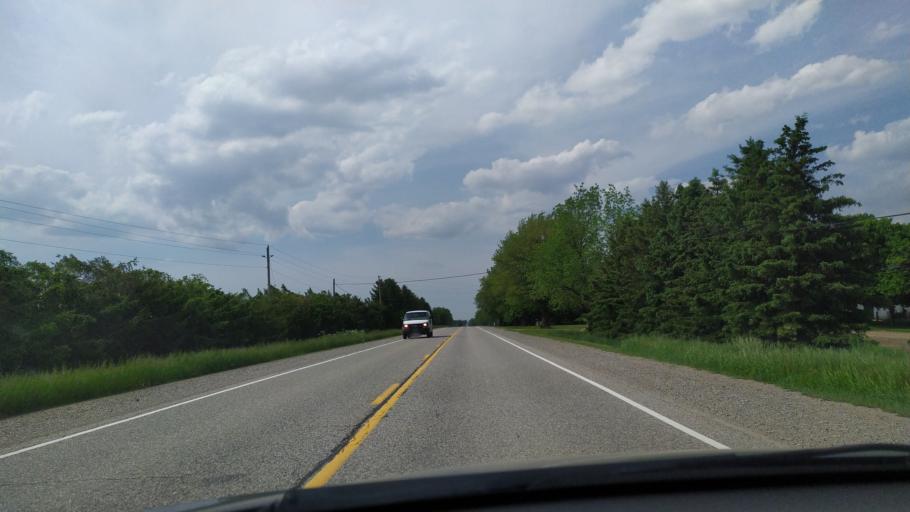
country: CA
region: Ontario
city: Dorchester
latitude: 43.1181
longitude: -81.0195
